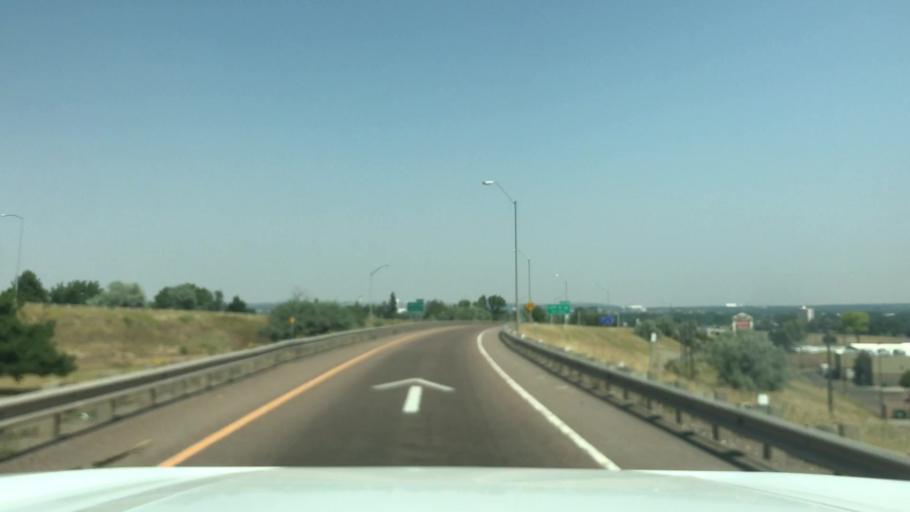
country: US
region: Montana
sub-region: Cascade County
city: Great Falls
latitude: 47.4840
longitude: -111.3449
